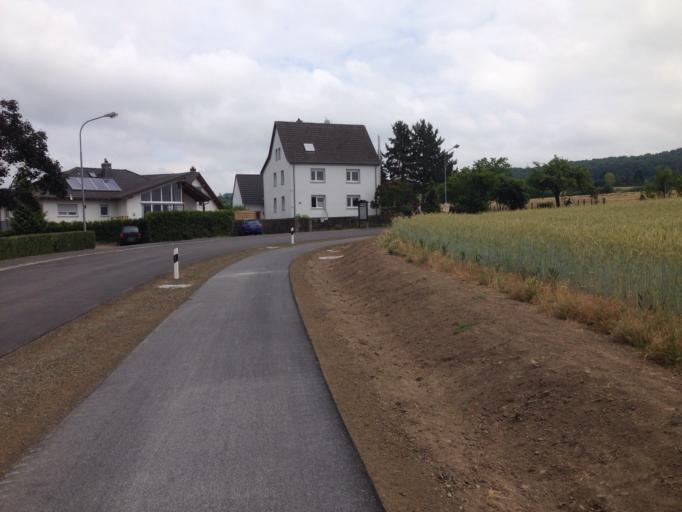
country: DE
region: Hesse
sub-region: Regierungsbezirk Giessen
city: Alten Buseck
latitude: 50.6079
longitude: 8.7534
